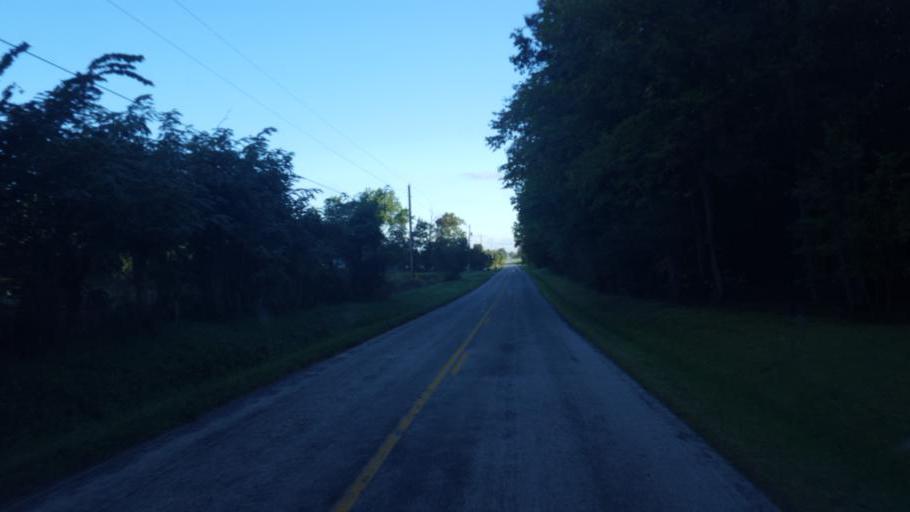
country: US
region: Ohio
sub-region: Huron County
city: New London
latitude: 41.0198
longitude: -82.2604
